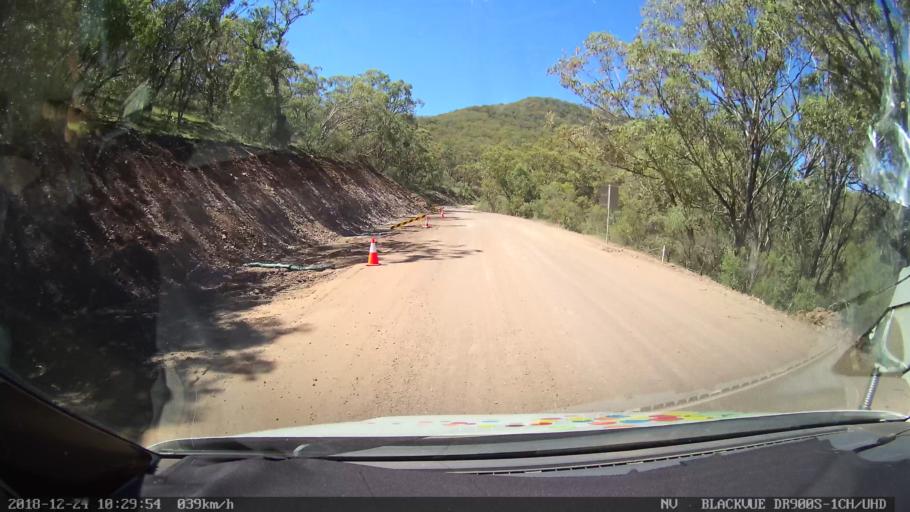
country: AU
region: New South Wales
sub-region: Upper Hunter Shire
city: Merriwa
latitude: -31.8340
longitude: 150.5267
